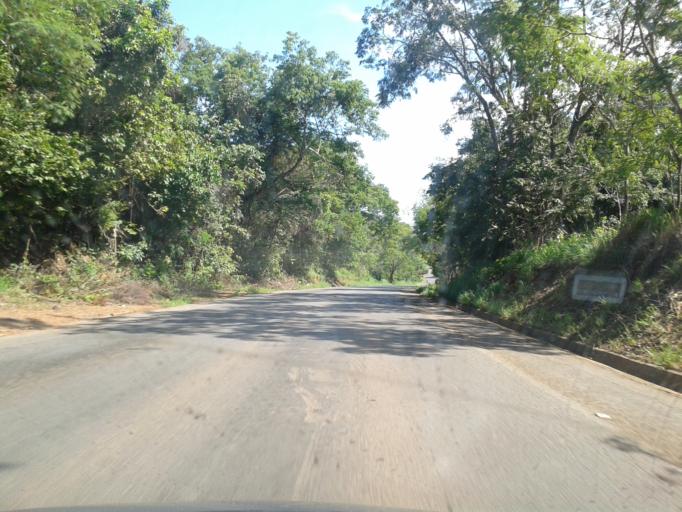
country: BR
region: Goias
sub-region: Piracanjuba
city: Piracanjuba
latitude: -17.2253
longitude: -48.7134
